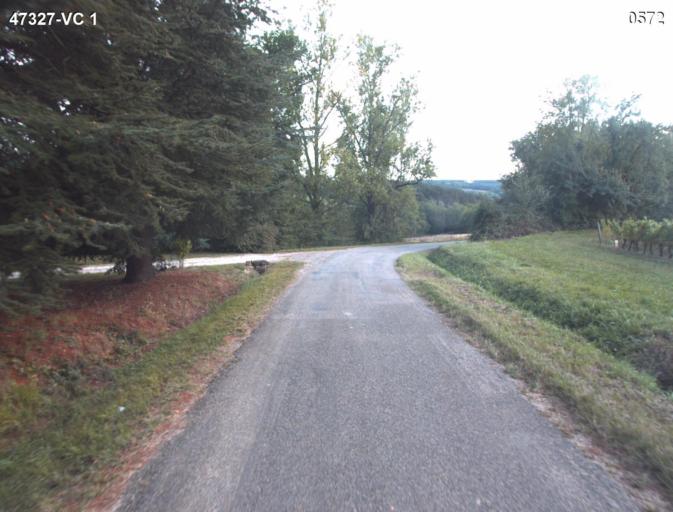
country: FR
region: Aquitaine
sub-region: Departement du Lot-et-Garonne
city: Barbaste
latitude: 44.1900
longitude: 0.2558
